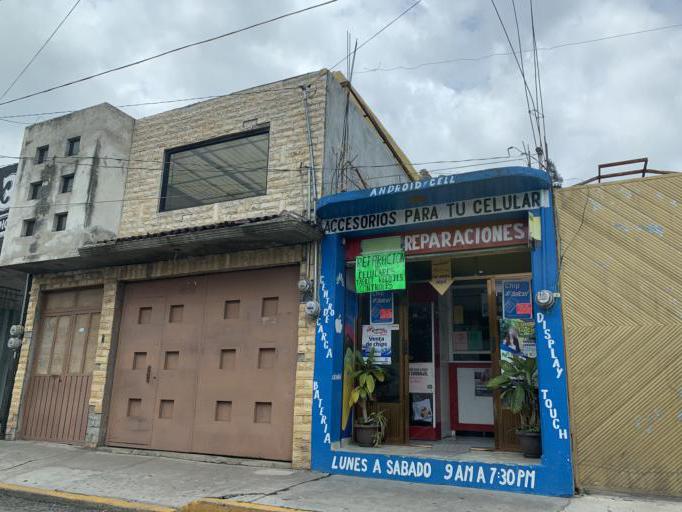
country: MX
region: Puebla
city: Huejotzingo
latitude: 19.1619
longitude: -98.4068
